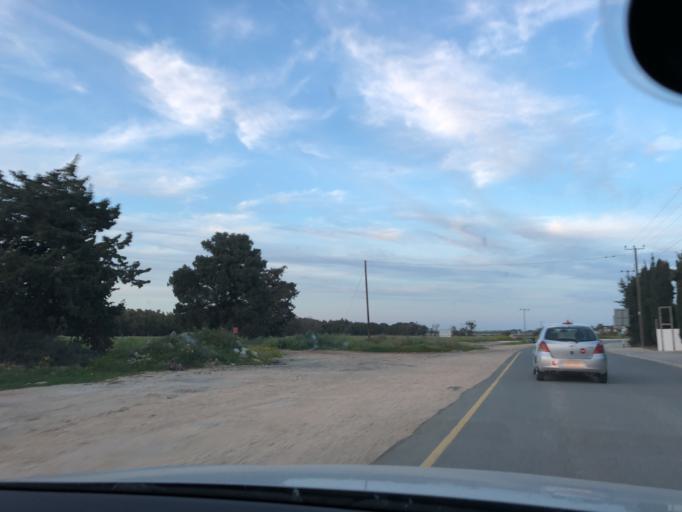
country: CY
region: Larnaka
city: Meneou
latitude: 34.8390
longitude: 33.6070
